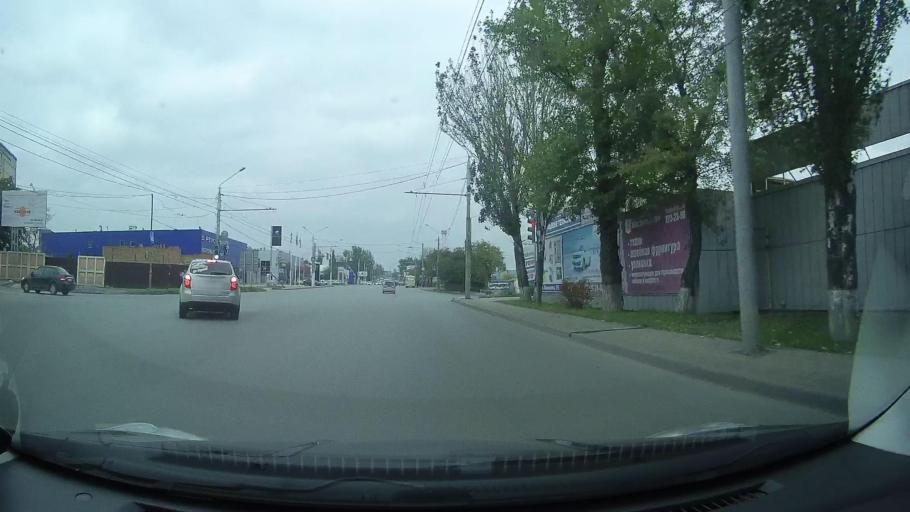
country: RU
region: Rostov
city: Severnyy
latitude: 47.2685
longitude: 39.6840
